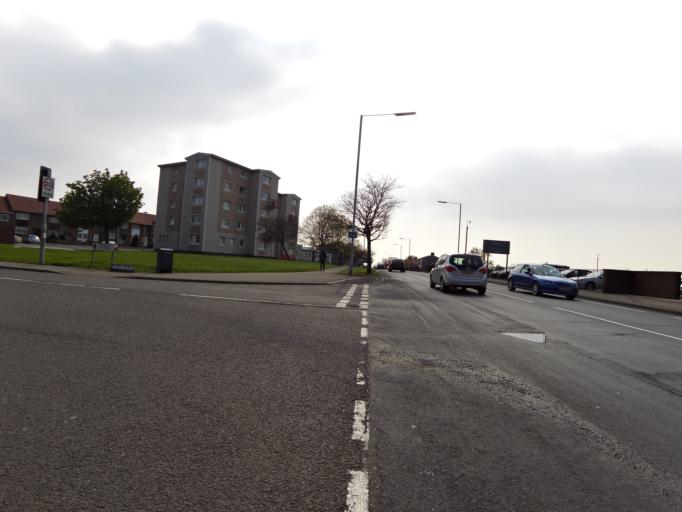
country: GB
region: Scotland
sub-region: Fife
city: Kirkcaldy
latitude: 56.1329
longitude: -3.1473
